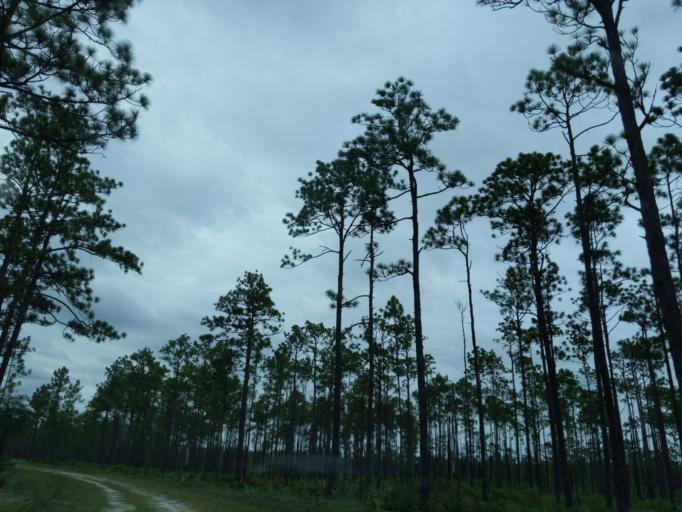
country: US
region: Florida
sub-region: Gadsden County
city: Midway
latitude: 30.3553
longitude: -84.4864
